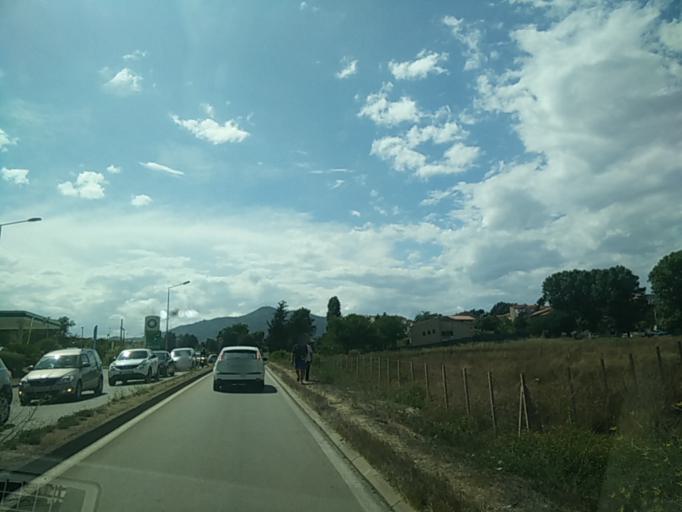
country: FR
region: Corsica
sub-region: Departement de la Corse-du-Sud
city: Afa
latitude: 41.9512
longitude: 8.7810
